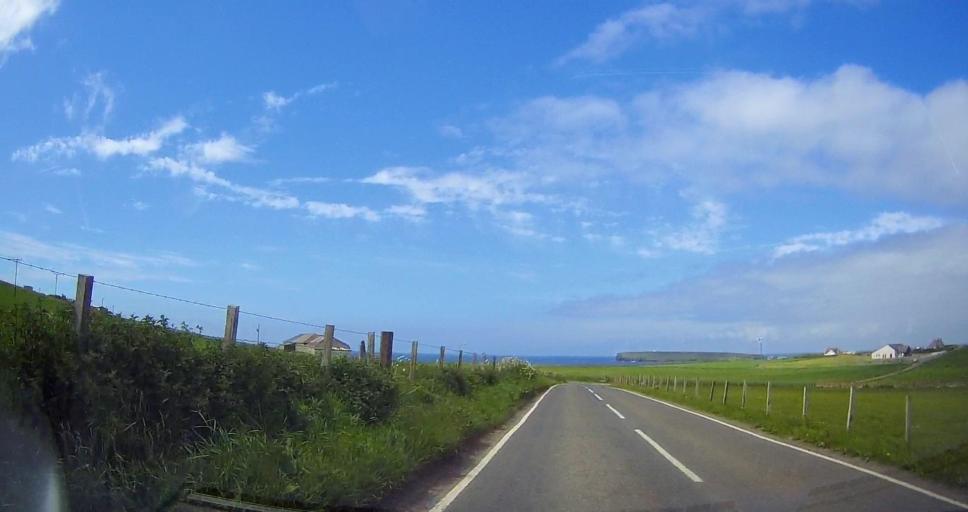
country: GB
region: Scotland
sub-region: Orkney Islands
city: Stromness
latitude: 59.1165
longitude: -3.3046
